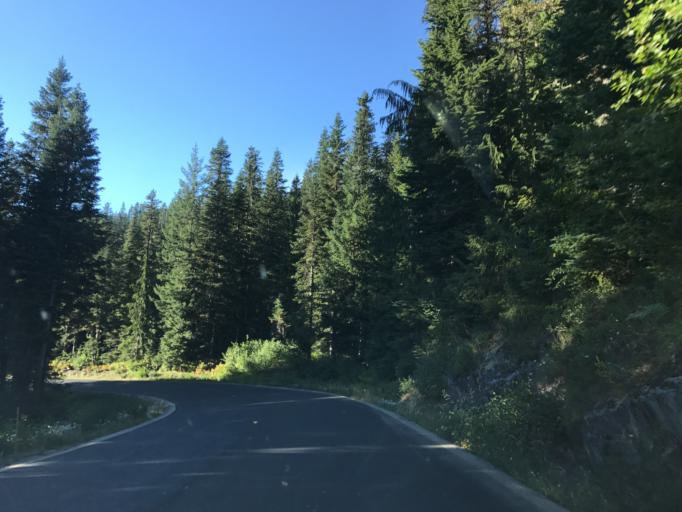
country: US
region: Washington
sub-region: Pierce County
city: Buckley
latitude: 46.7758
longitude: -121.7531
